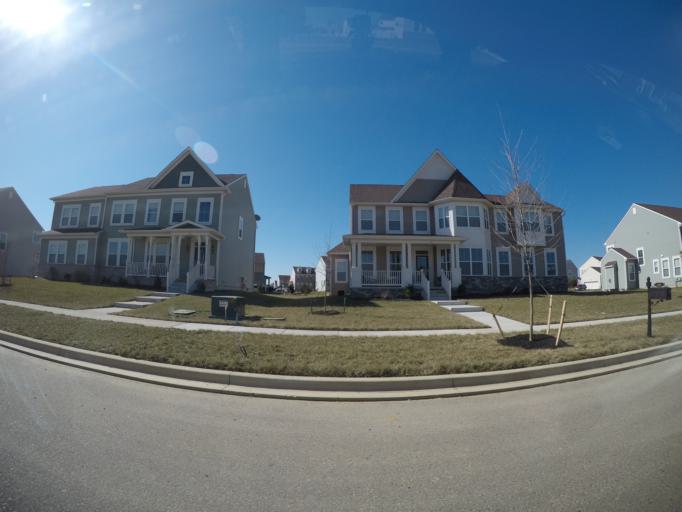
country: US
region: Delaware
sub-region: New Castle County
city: Middletown
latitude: 39.5135
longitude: -75.6654
